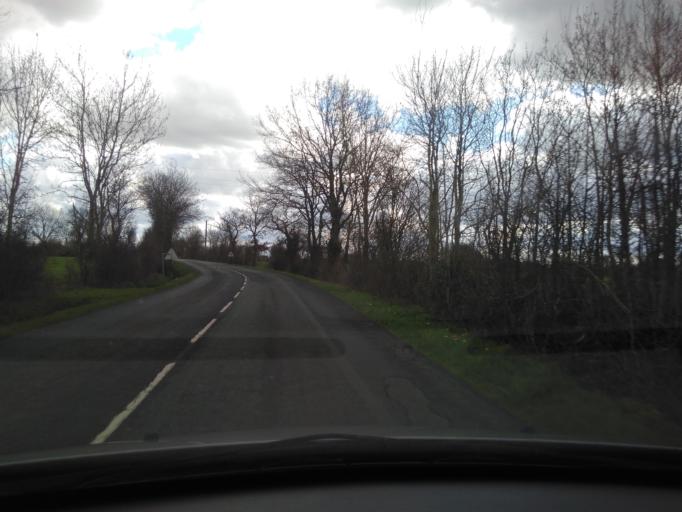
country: FR
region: Pays de la Loire
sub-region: Departement de la Vendee
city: Saint-Martin-des-Noyers
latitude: 46.7398
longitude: -1.1861
